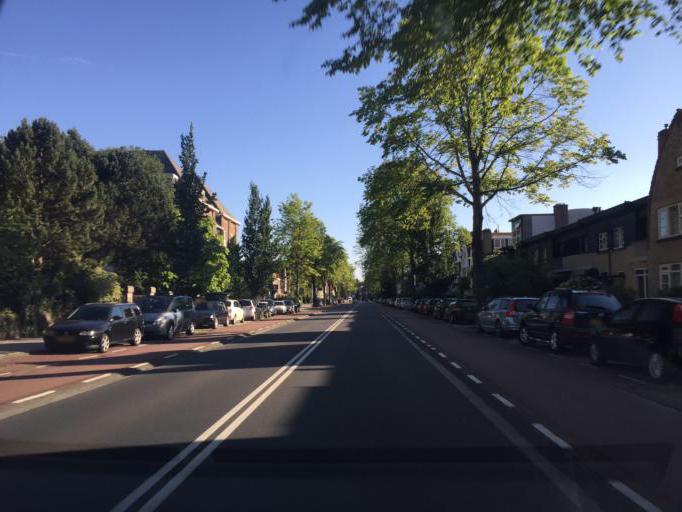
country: NL
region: North Holland
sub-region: Gemeente Bloemendaal
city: Bloemendaal
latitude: 52.3954
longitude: 4.6264
